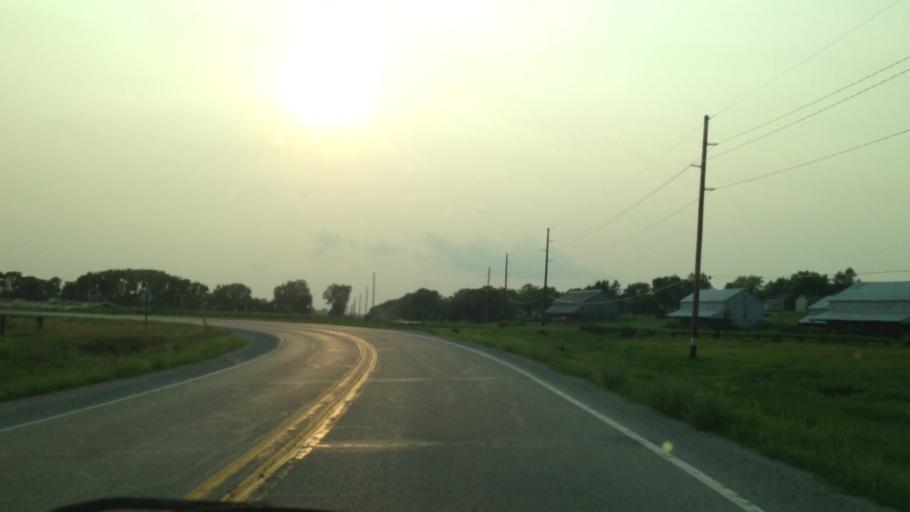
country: US
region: Iowa
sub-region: Iowa County
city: Marengo
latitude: 41.8053
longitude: -91.9603
